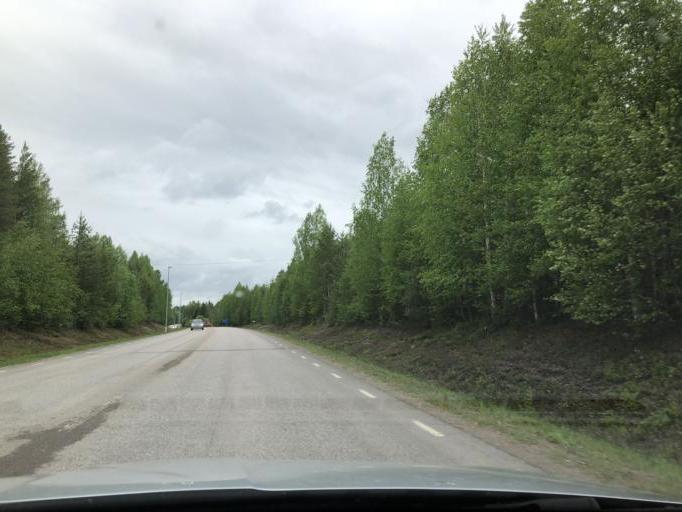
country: SE
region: Norrbotten
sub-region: Pitea Kommun
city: Bergsviken
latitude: 65.3821
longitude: 21.3369
